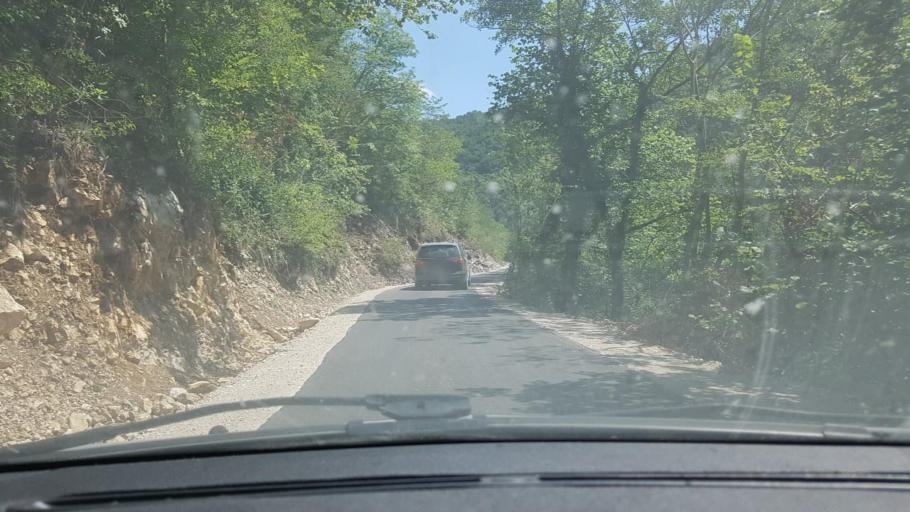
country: BA
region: Federation of Bosnia and Herzegovina
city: Orasac
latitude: 44.6278
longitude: 16.0448
